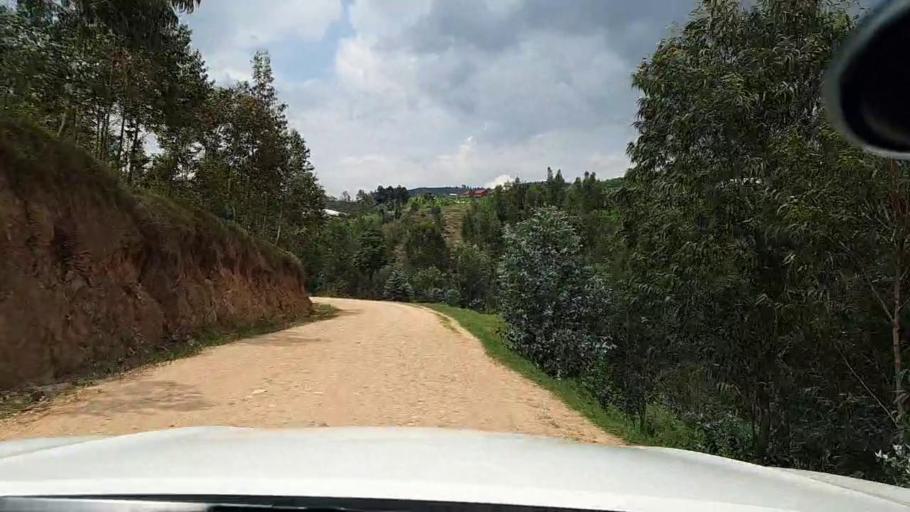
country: RW
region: Western Province
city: Kibuye
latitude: -2.1190
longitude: 29.4247
